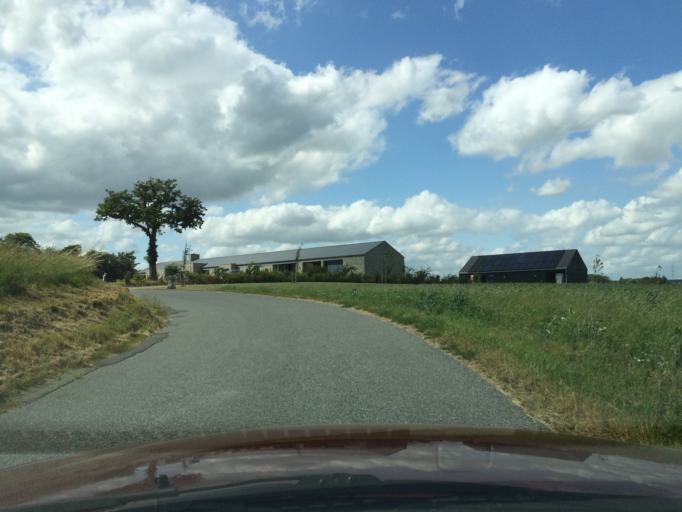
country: DK
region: Central Jutland
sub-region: Skanderborg Kommune
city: Galten
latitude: 56.1605
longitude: 9.8984
